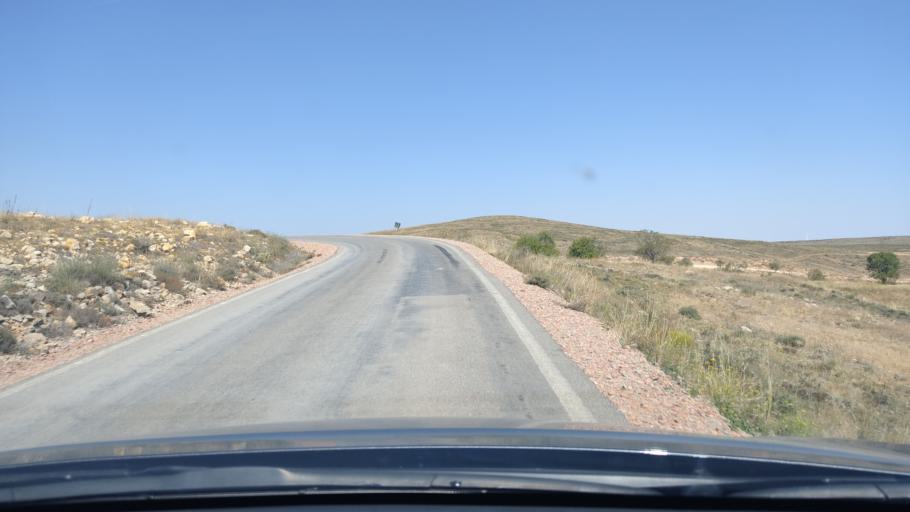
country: ES
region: Aragon
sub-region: Provincia de Teruel
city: Monforte de Moyuela
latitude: 41.0417
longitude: -0.9841
